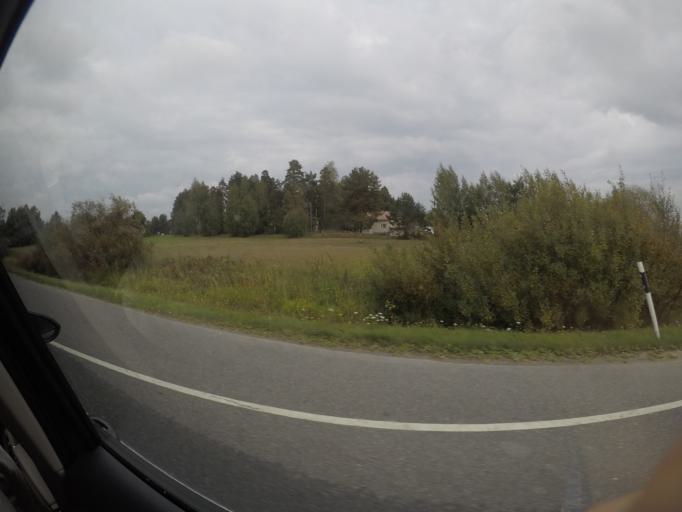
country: FI
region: Haeme
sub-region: Haemeenlinna
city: Parola
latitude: 61.0449
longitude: 24.3985
